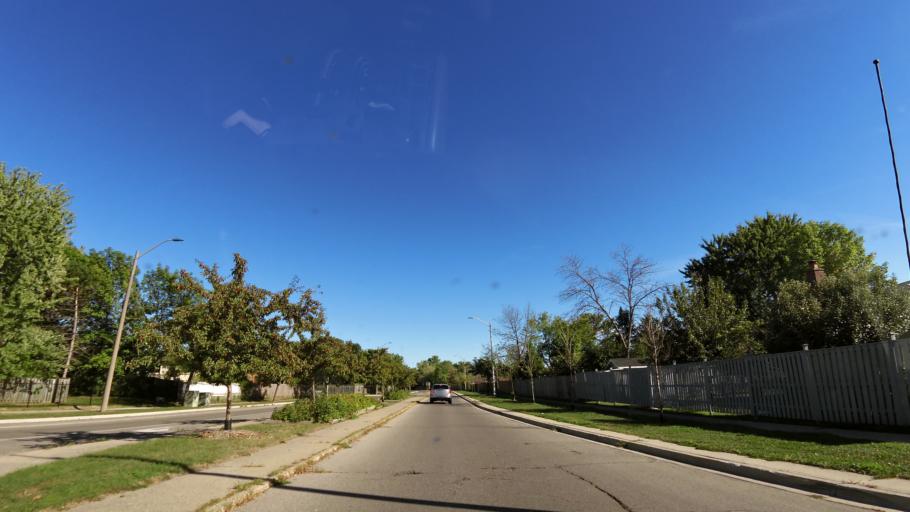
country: CA
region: Ontario
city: Mississauga
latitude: 43.5930
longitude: -79.6209
